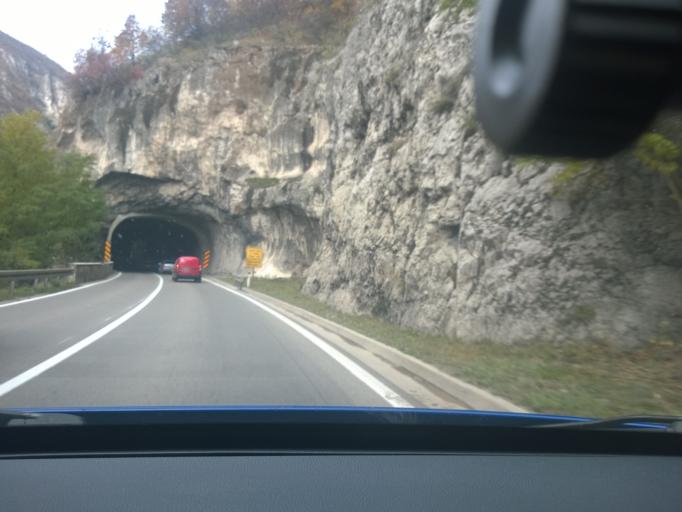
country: RS
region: Central Serbia
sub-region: Nisavski Okrug
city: Svrljig
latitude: 43.3219
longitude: 22.1713
